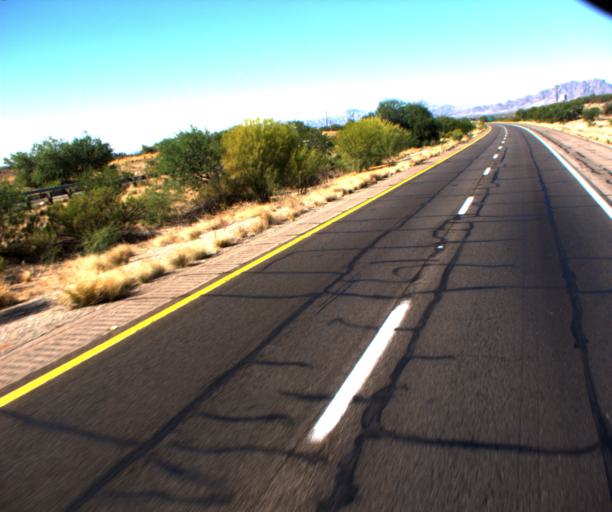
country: US
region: Arizona
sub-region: Pima County
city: Arivaca Junction
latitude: 31.7352
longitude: -111.0535
